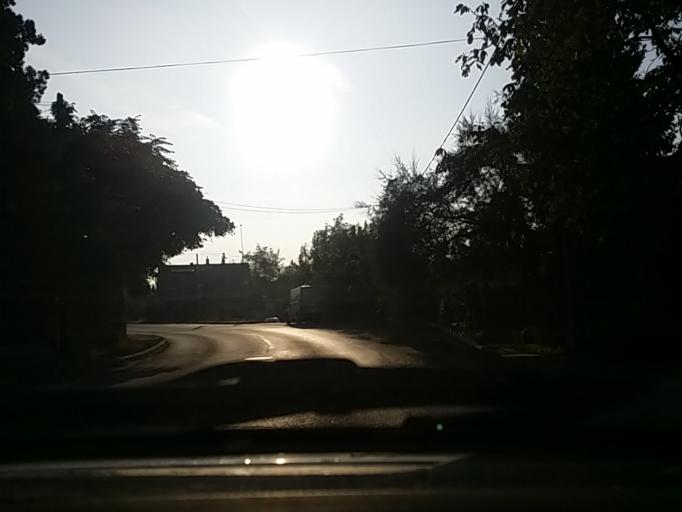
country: HU
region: Pest
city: Szentendre
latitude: 47.6713
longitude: 19.0709
